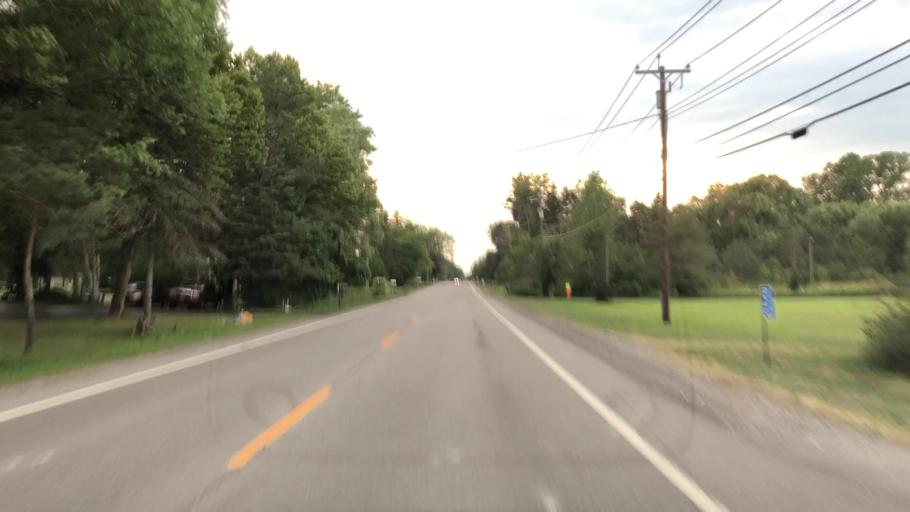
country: US
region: New York
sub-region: Erie County
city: Elma Center
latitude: 42.8391
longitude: -78.6522
